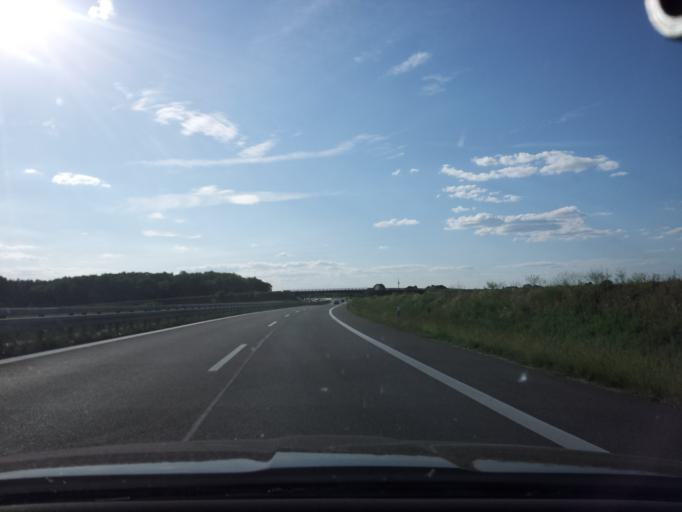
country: DE
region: Brandenburg
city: Stahnsdorf
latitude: 52.3656
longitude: 13.2193
